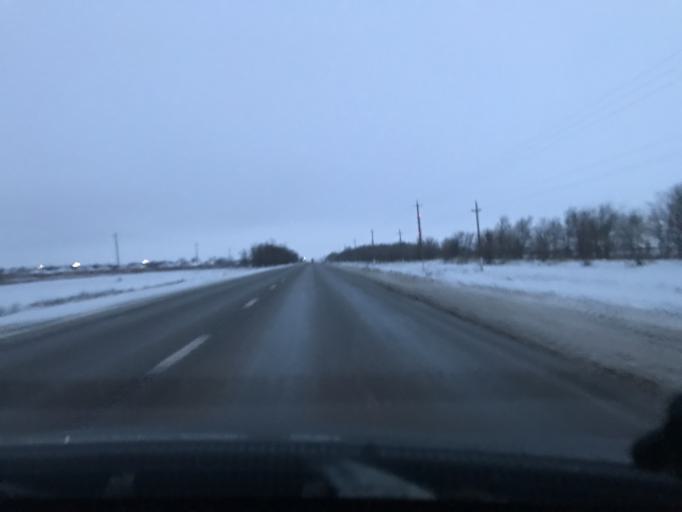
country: RU
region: Rostov
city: Letnik
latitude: 45.9123
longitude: 41.2924
